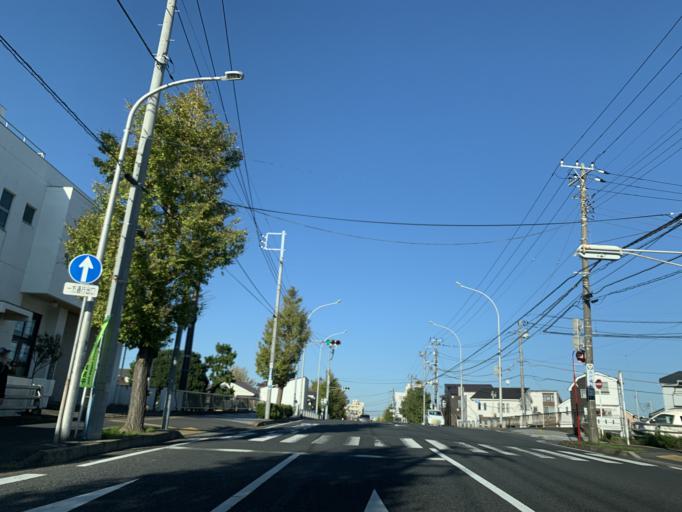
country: JP
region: Tokyo
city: Urayasu
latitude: 35.6588
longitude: 139.8966
